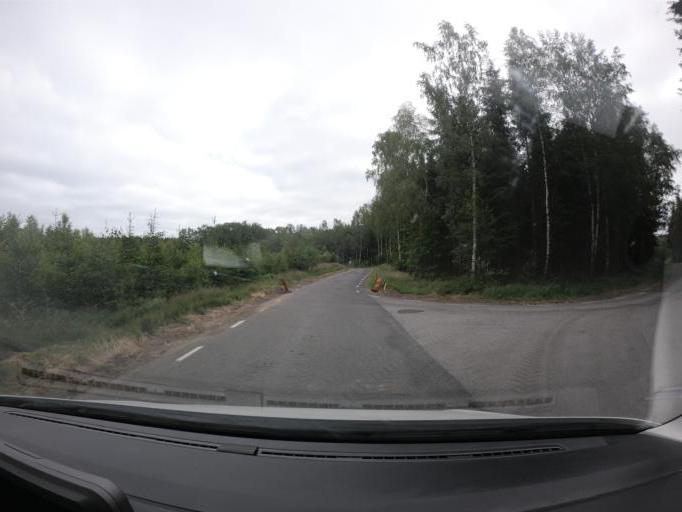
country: SE
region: Skane
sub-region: Hassleholms Kommun
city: Sosdala
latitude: 56.0252
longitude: 13.5799
